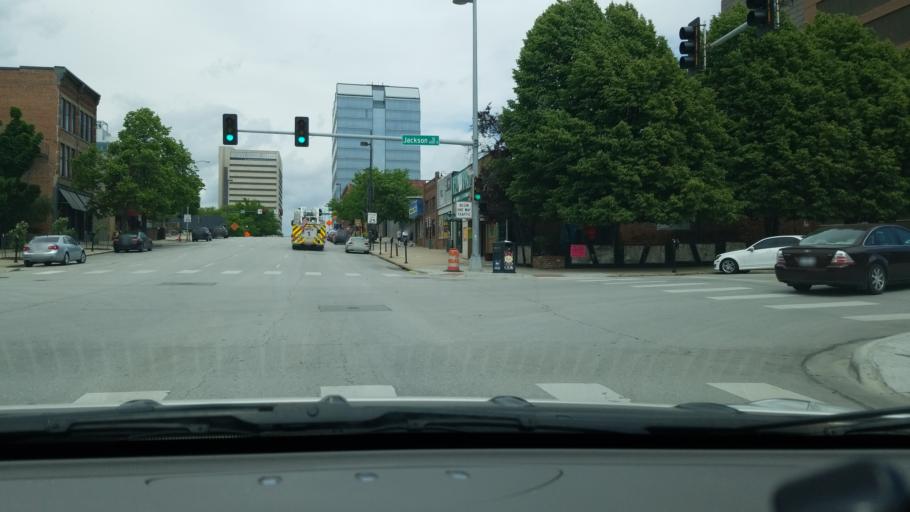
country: US
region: Nebraska
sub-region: Douglas County
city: Omaha
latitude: 41.2542
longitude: -95.9332
